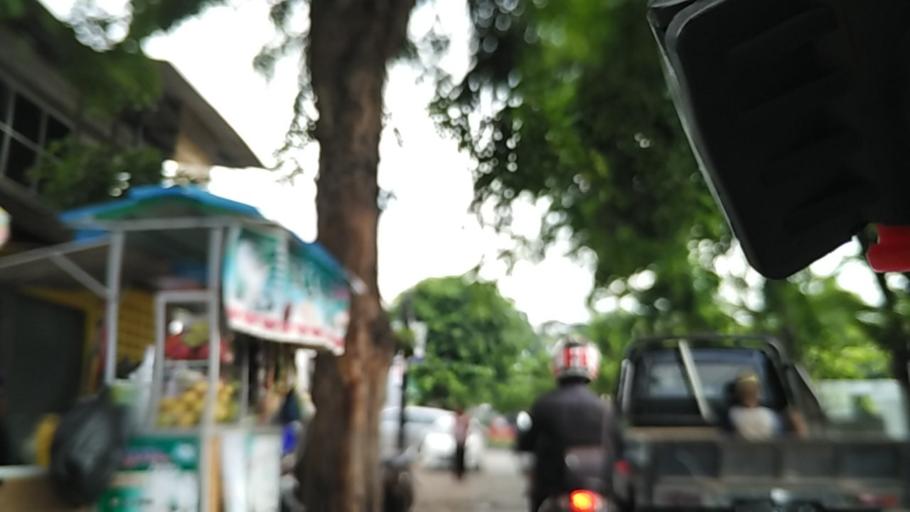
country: ID
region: Central Java
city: Semarang
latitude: -6.9943
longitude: 110.4138
